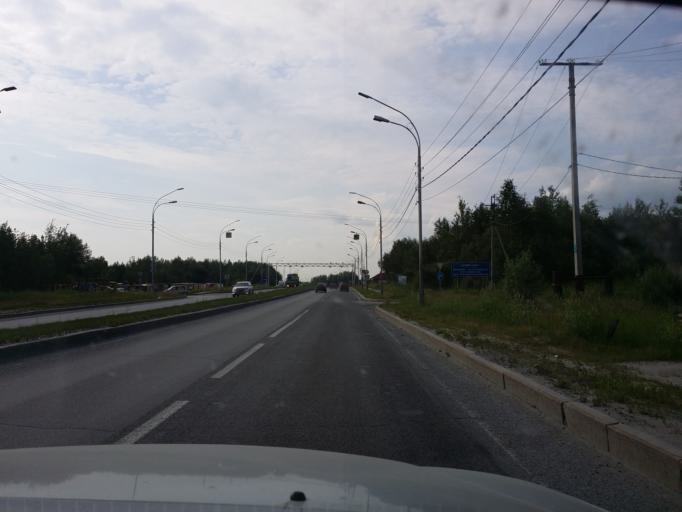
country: RU
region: Khanty-Mansiyskiy Avtonomnyy Okrug
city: Nizhnevartovsk
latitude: 60.9723
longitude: 76.5253
